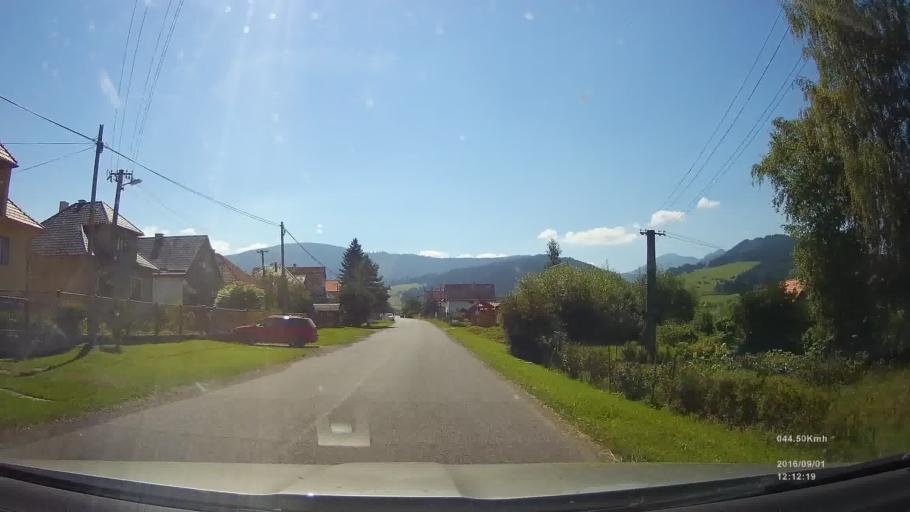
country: SK
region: Zilinsky
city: Ruzomberok
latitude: 49.0584
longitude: 19.4310
